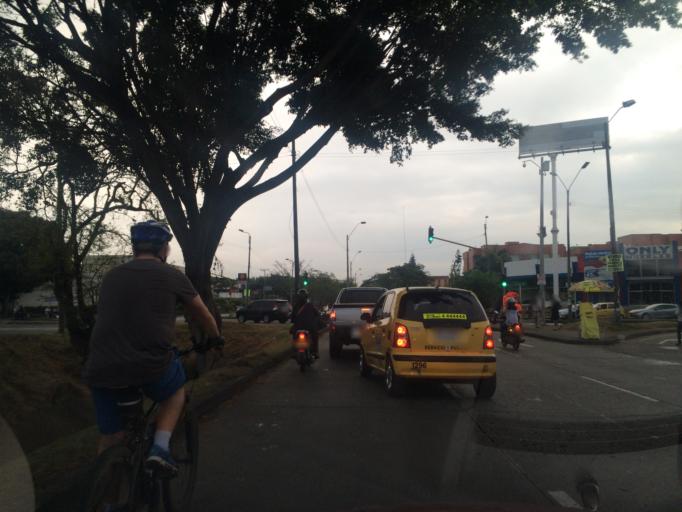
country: CO
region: Valle del Cauca
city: Cali
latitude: 3.4047
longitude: -76.5357
